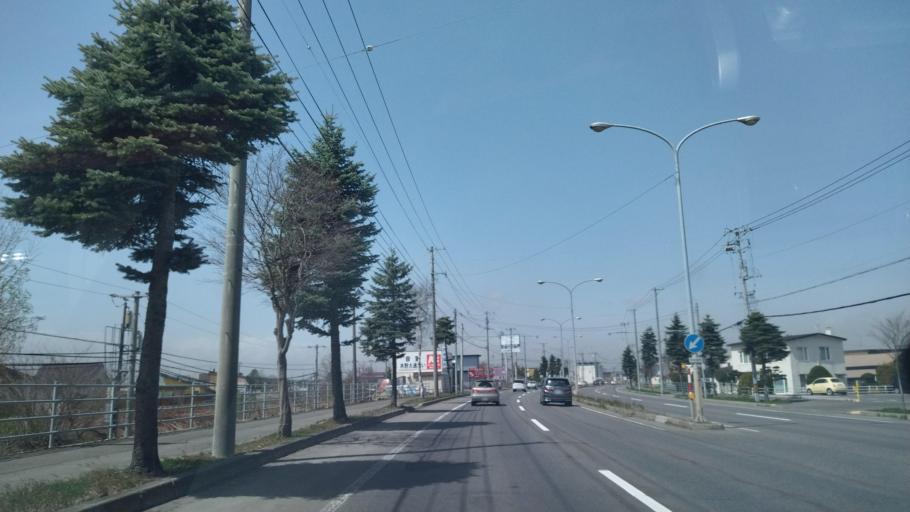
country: JP
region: Hokkaido
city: Obihiro
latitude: 42.9156
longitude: 143.2505
